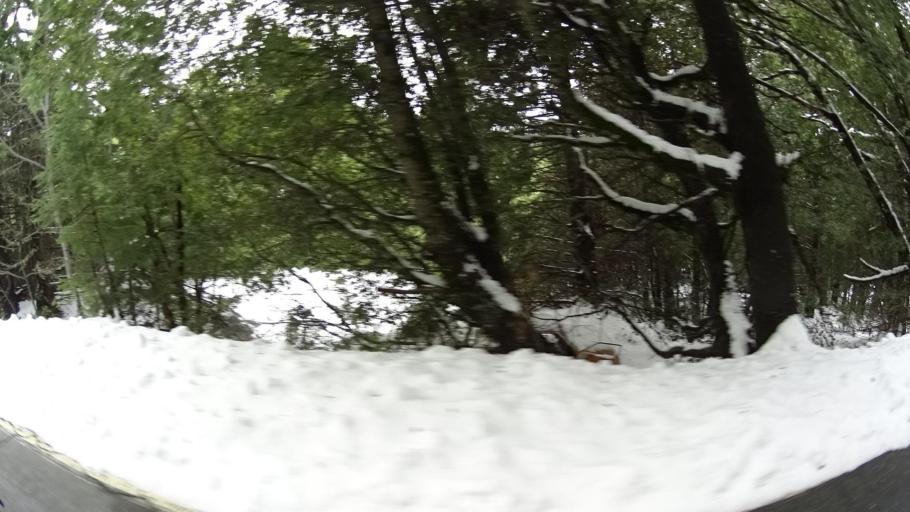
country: US
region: California
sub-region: Humboldt County
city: Willow Creek
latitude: 40.8676
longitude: -123.7445
